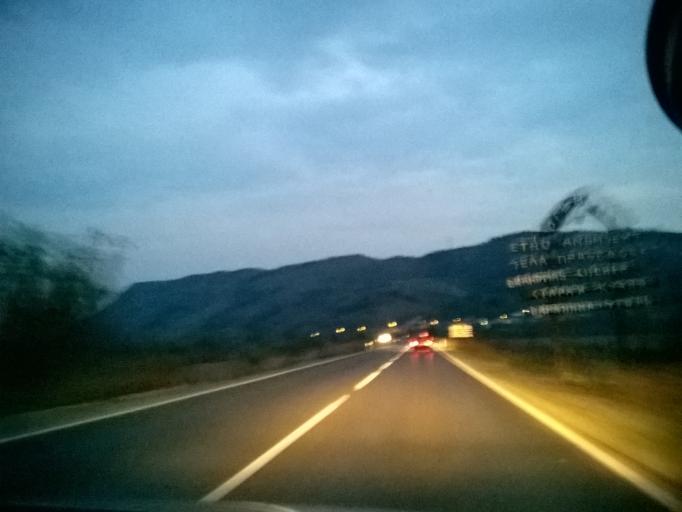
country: ME
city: Spuz
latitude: 42.4651
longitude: 19.1753
